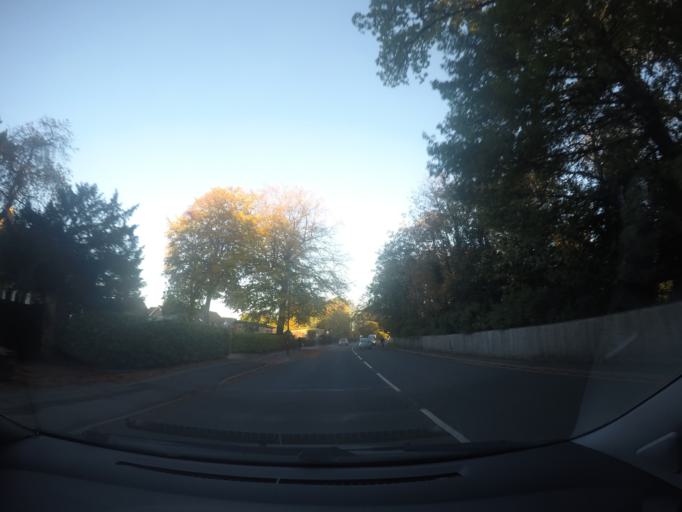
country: GB
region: England
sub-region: City of York
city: York
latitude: 53.9722
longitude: -1.1034
